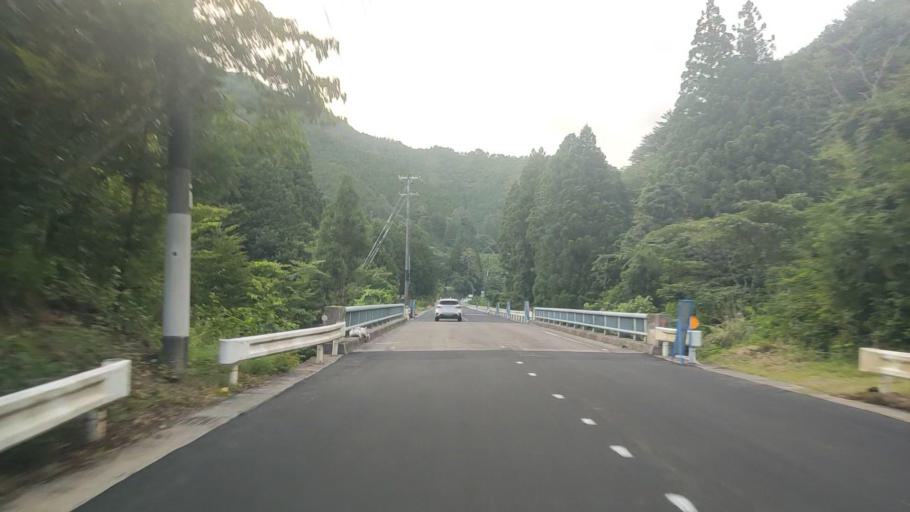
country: JP
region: Wakayama
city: Tanabe
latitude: 33.8321
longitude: 135.6517
